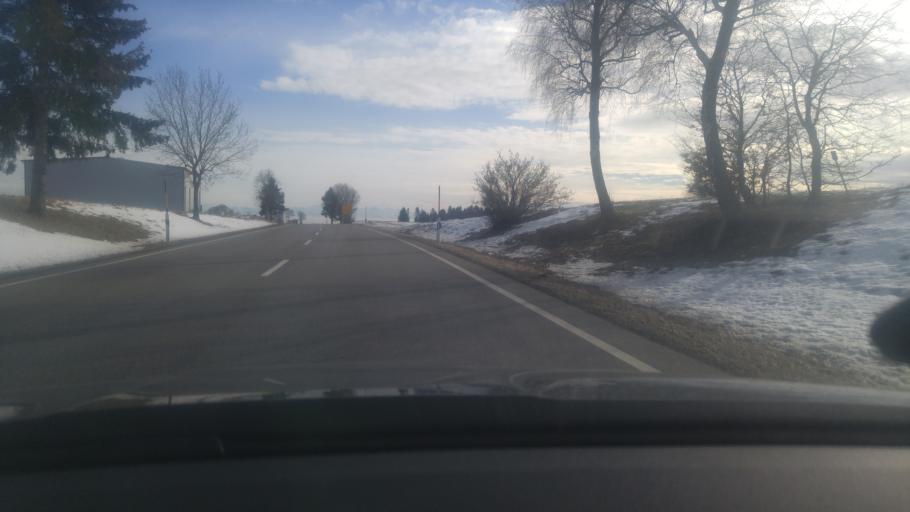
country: DE
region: Baden-Wuerttemberg
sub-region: Freiburg Region
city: Hochenschwand
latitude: 47.7081
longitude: 8.1434
